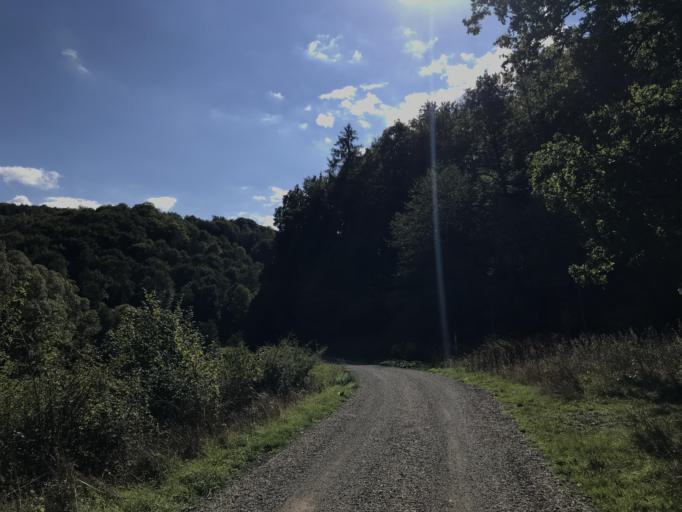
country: DE
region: Hesse
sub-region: Regierungsbezirk Kassel
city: Sachsenhausen
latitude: 51.2252
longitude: 9.0311
